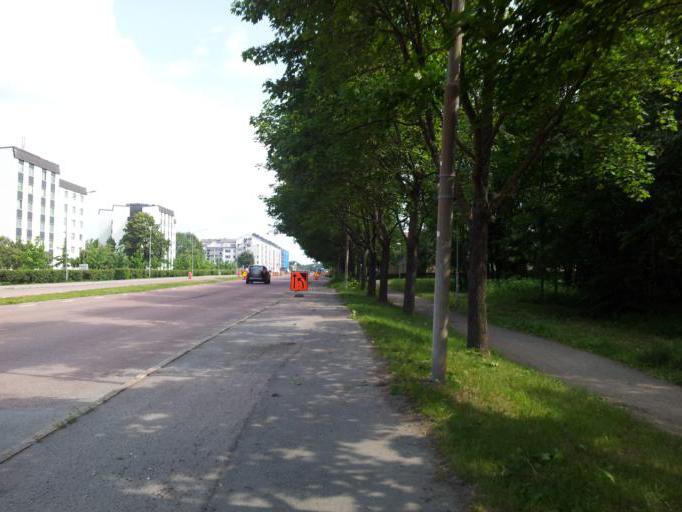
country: SE
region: Uppsala
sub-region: Uppsala Kommun
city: Uppsala
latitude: 59.8665
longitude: 17.6415
